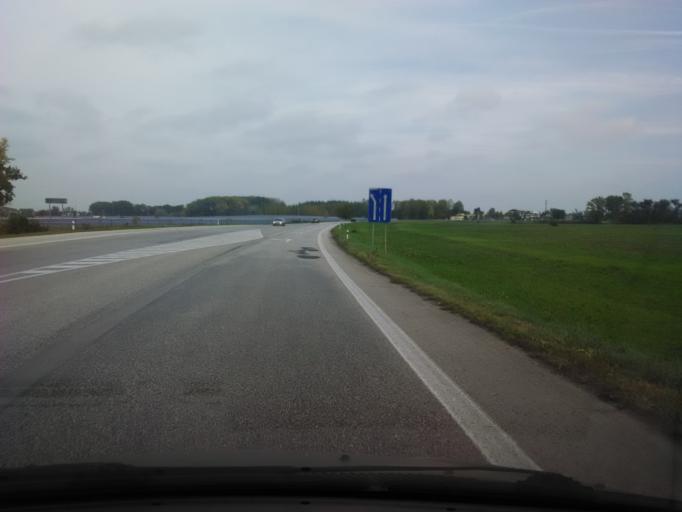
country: SK
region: Nitriansky
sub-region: Okres Komarno
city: Hurbanovo
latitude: 47.8593
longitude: 18.1760
